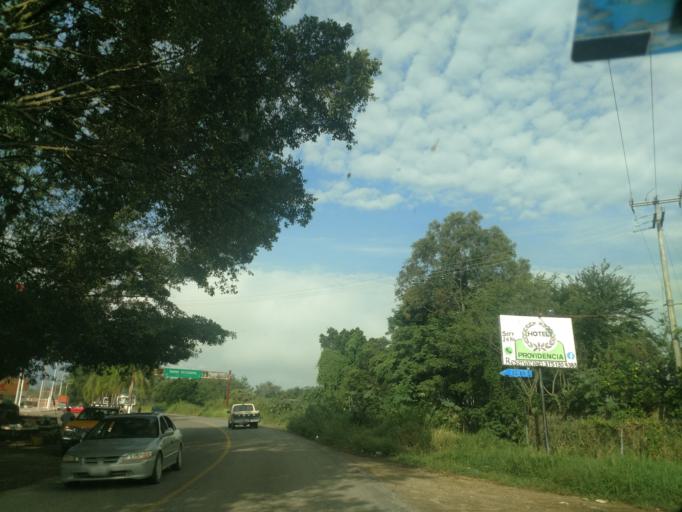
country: MX
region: Jalisco
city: Ameca
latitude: 20.5385
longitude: -104.0464
